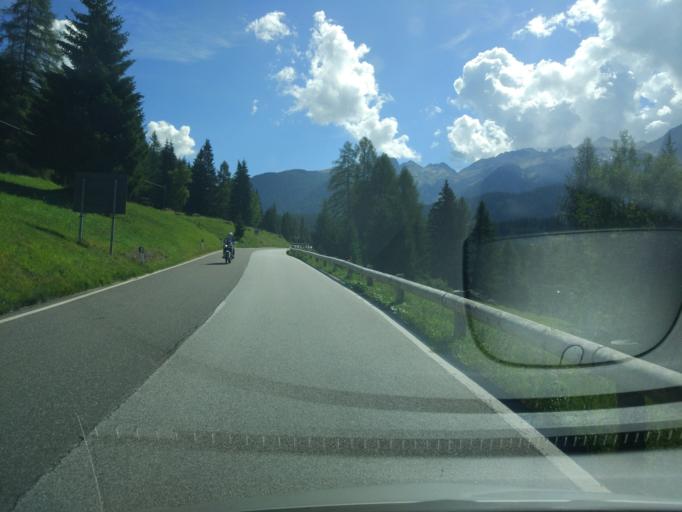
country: IT
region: Trentino-Alto Adige
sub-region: Provincia di Trento
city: Moena
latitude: 46.3091
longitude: 11.6830
